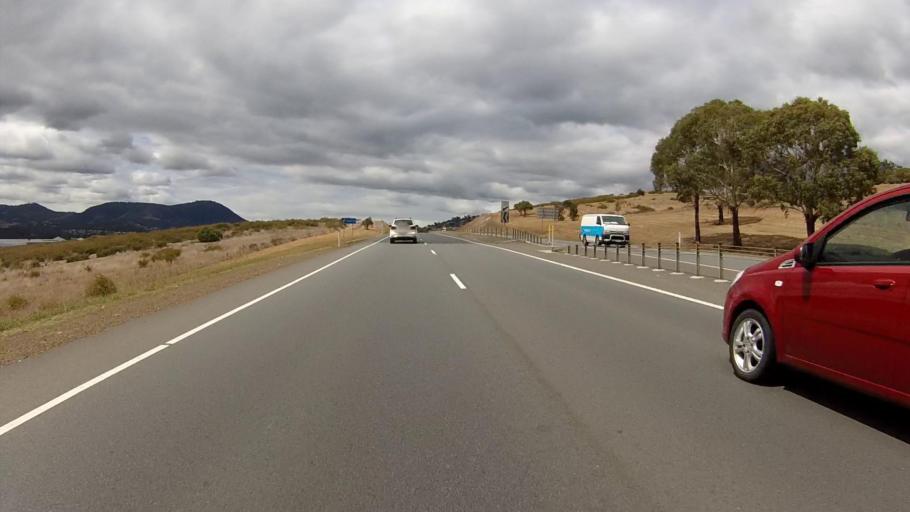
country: AU
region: Tasmania
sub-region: Glenorchy
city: Granton
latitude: -42.7587
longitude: 147.2314
